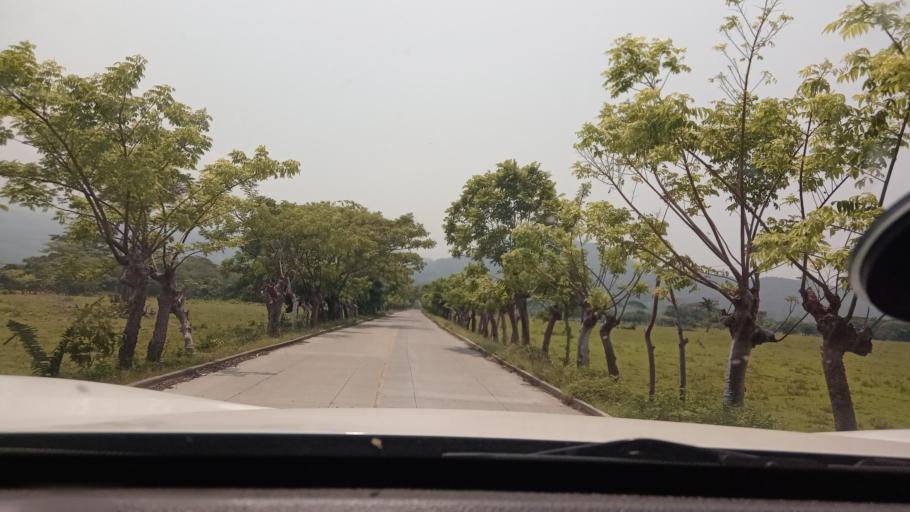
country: MX
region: Veracruz
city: Catemaco
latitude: 18.5627
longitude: -95.0465
